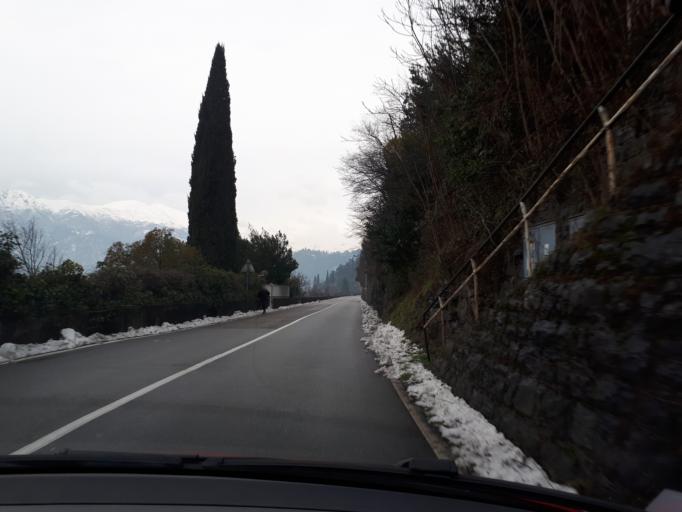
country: IT
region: Lombardy
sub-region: Provincia di Lecco
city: Varenna
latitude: 45.9870
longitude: 9.2923
